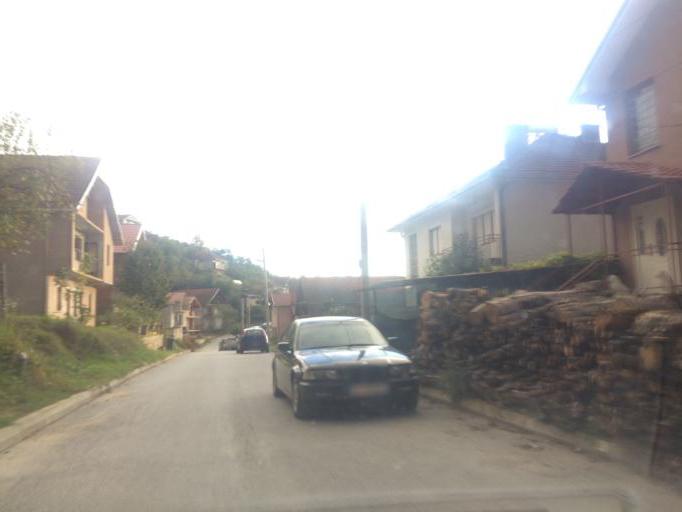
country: MK
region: Makedonska Kamenica
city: Makedonska Kamenica
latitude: 42.0162
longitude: 22.5924
